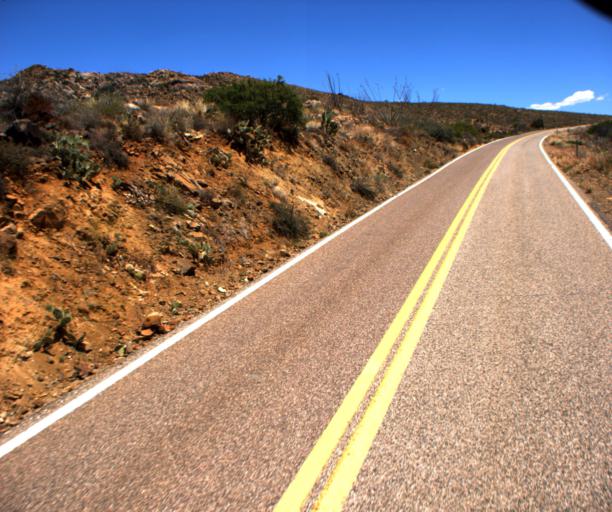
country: US
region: Arizona
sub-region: Yavapai County
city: Bagdad
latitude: 34.4457
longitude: -112.9582
